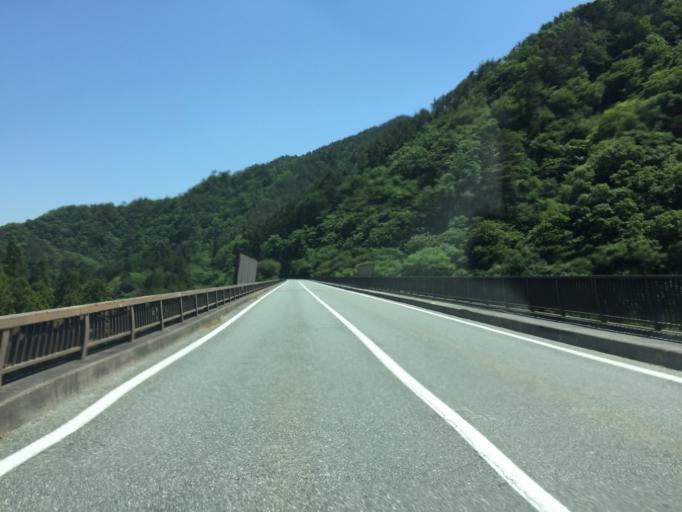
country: JP
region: Fukushima
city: Namie
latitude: 37.5102
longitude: 140.8946
